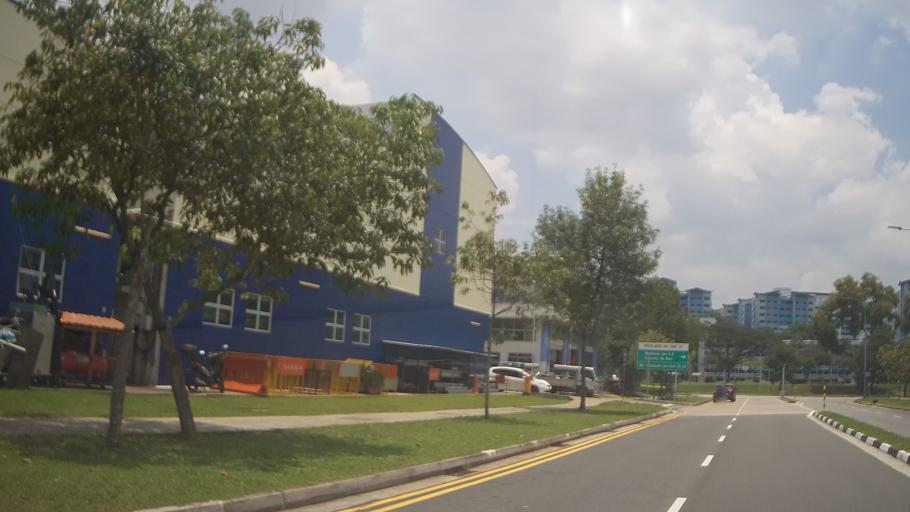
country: MY
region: Johor
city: Johor Bahru
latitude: 1.4487
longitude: 103.7931
